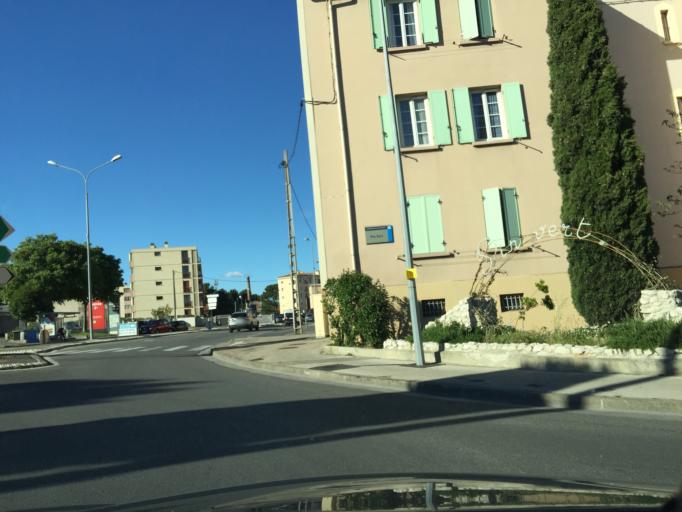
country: FR
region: Provence-Alpes-Cote d'Azur
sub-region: Departement des Bouches-du-Rhone
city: Aubagne
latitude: 43.3009
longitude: 5.5702
